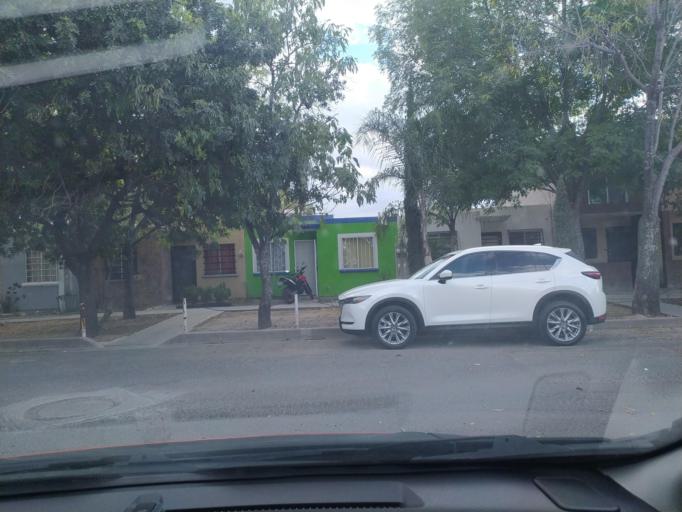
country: LA
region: Oudomxai
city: Muang La
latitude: 21.0269
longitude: 101.8277
